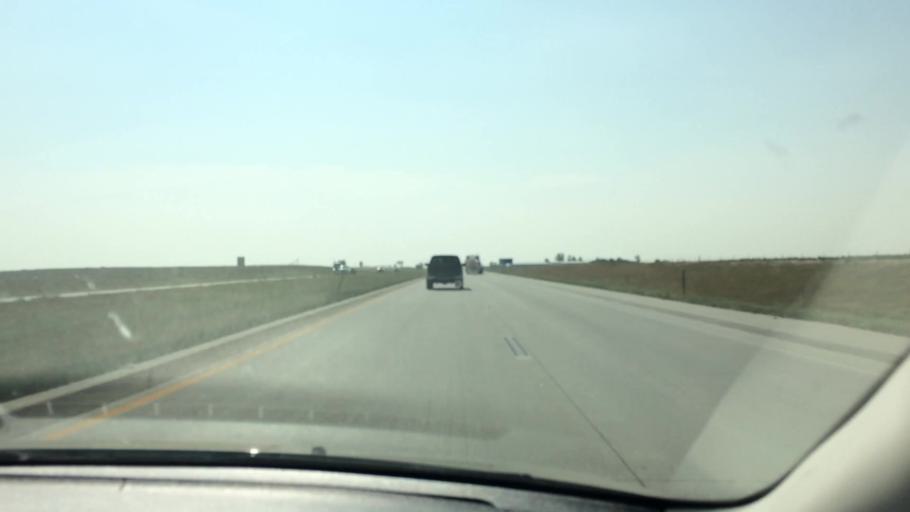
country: US
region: Colorado
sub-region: Adams County
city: Bennett
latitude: 39.7386
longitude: -104.5113
